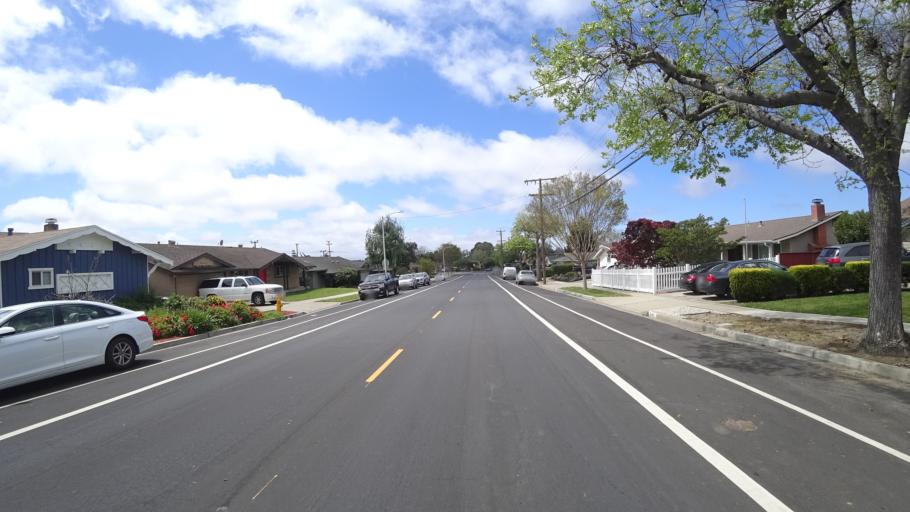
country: US
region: California
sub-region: Alameda County
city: Union City
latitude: 37.6285
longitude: -122.0414
